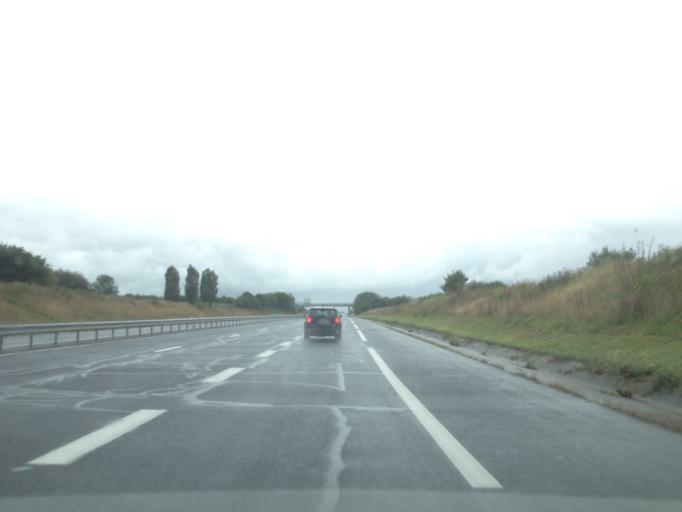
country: FR
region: Lower Normandy
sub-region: Departement du Calvados
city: Port-en-Bessin-Huppain
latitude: 49.2883
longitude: -0.7599
